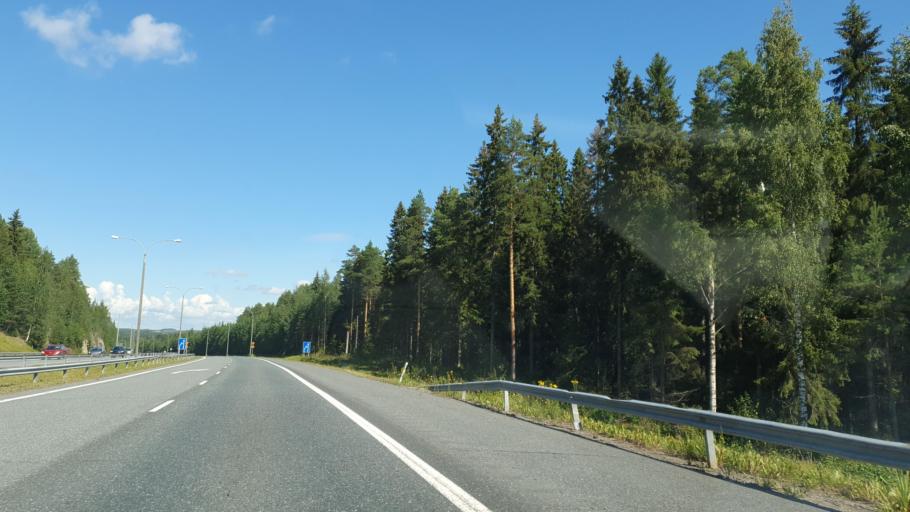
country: FI
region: Northern Savo
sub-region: Ylae-Savo
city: Iisalmi
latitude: 63.5542
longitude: 27.2562
